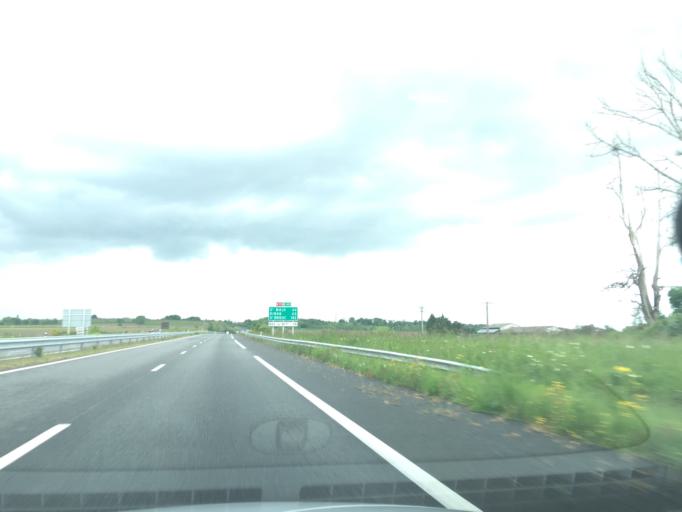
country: FR
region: Brittany
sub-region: Departement d'Ille-et-Vilaine
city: Pleine-Fougeres
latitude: 48.5631
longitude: -1.5505
